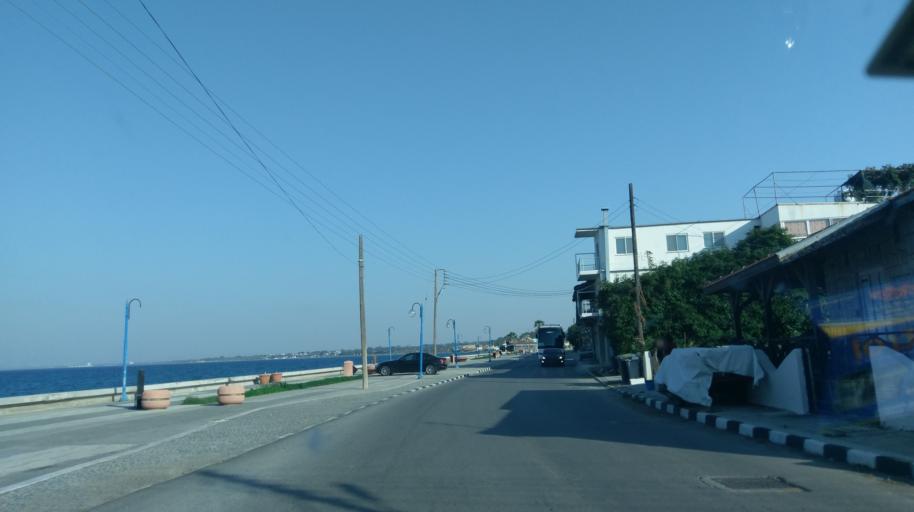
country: CY
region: Lefkosia
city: Lefka
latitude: 35.1423
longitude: 32.8195
